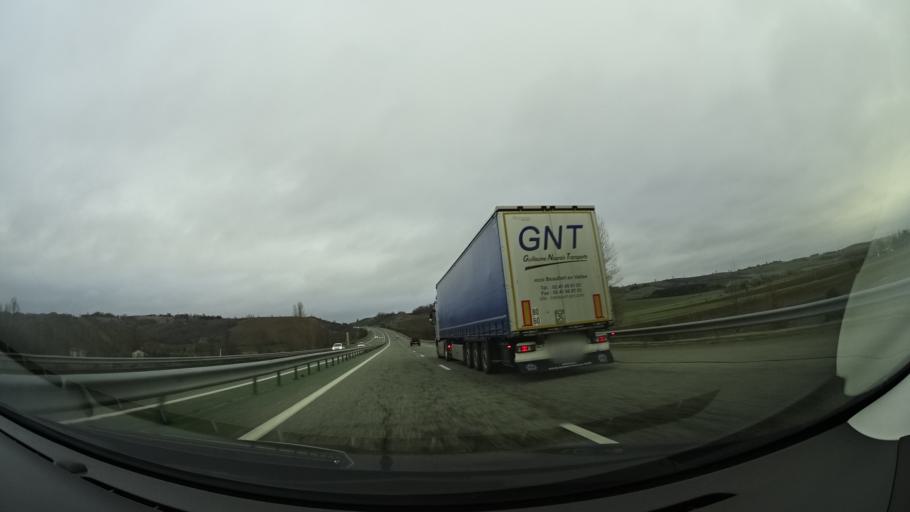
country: FR
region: Midi-Pyrenees
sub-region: Departement de l'Ariege
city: Mazeres
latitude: 43.2668
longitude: 1.6666
